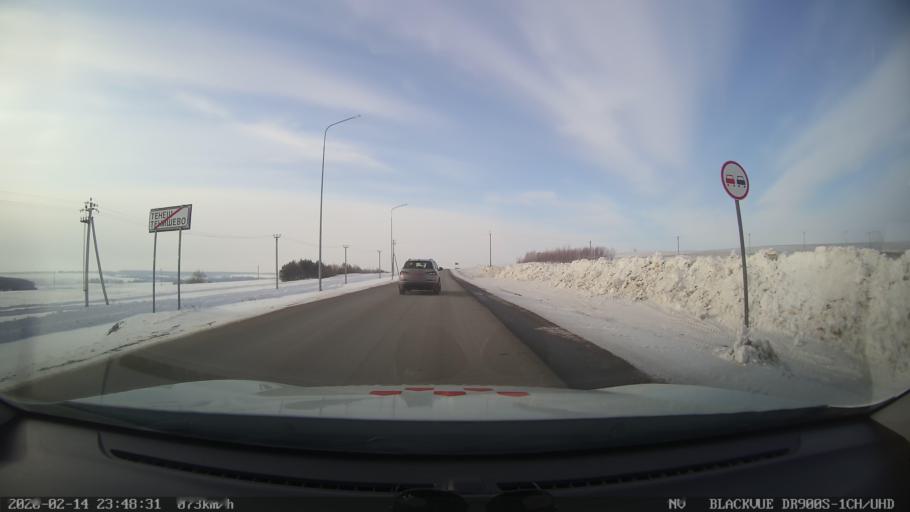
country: RU
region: Tatarstan
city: Kuybyshevskiy Zaton
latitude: 55.2483
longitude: 49.2013
